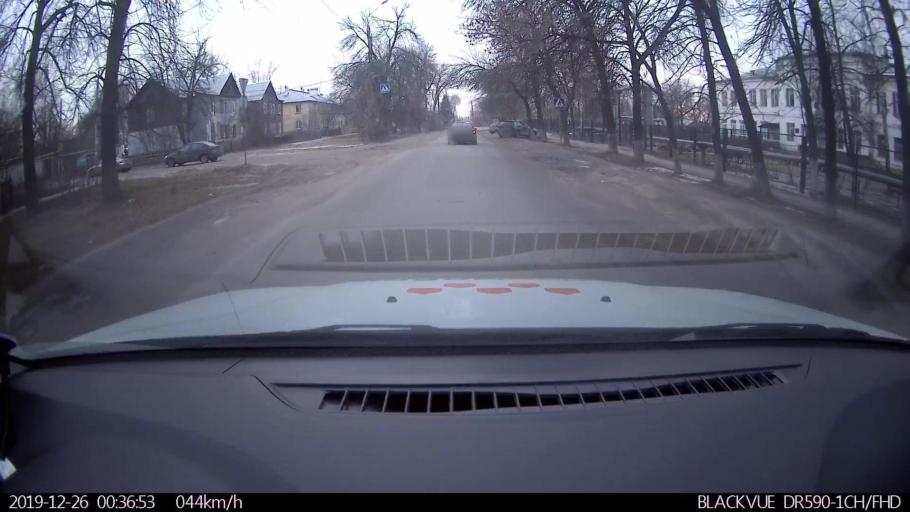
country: RU
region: Nizjnij Novgorod
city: Nizhniy Novgorod
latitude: 56.2908
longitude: 43.9055
